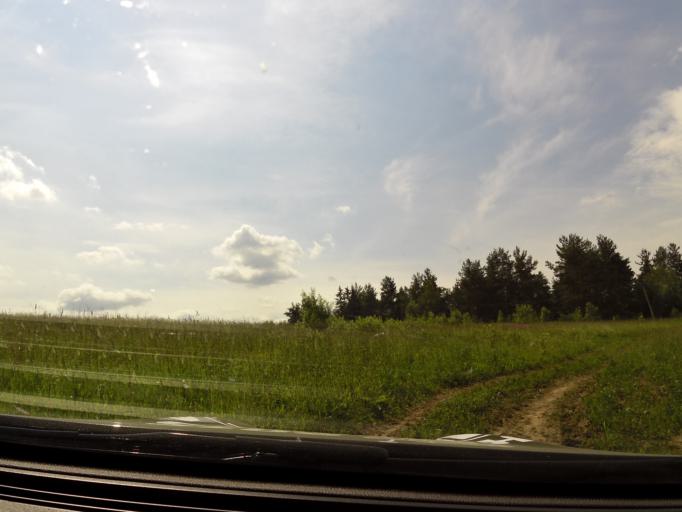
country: RU
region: Kostroma
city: Galich
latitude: 58.3727
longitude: 42.3960
